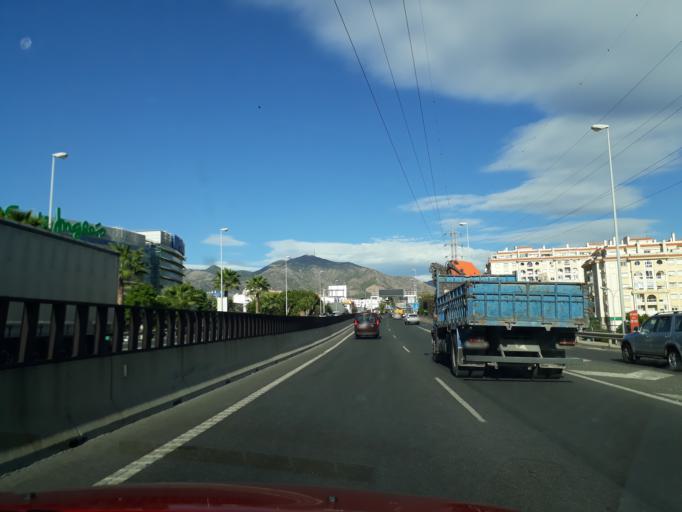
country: ES
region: Andalusia
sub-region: Provincia de Malaga
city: Fuengirola
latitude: 36.5469
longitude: -4.6319
